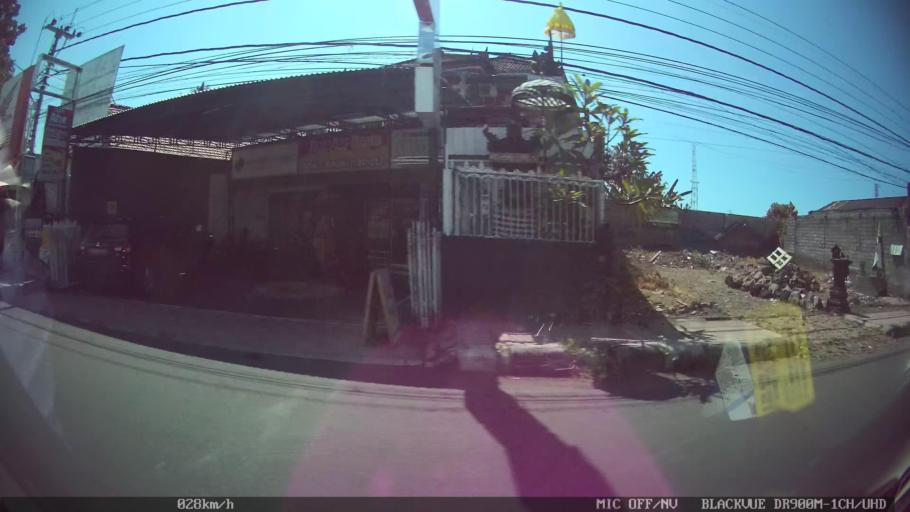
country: ID
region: Bali
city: Banjar Banyualit
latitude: -8.1590
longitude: 115.0317
